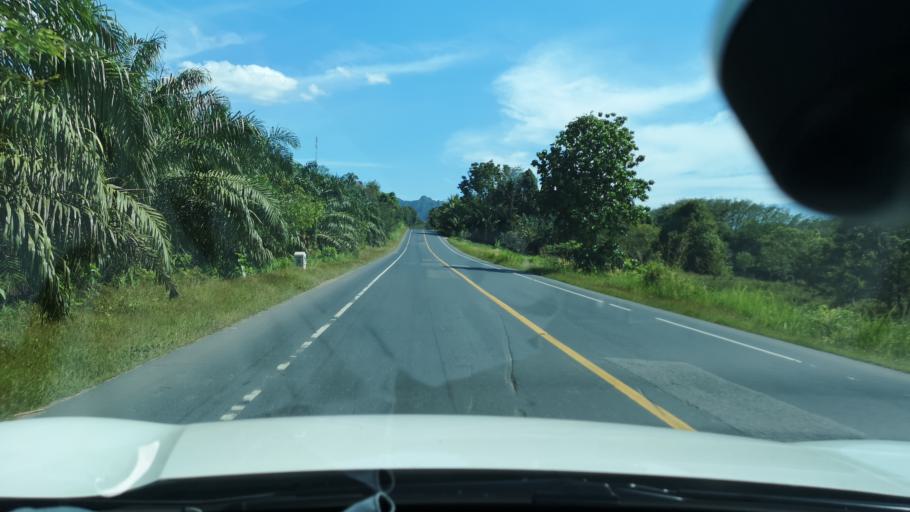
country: TH
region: Phangnga
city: Phang Nga
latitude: 8.5382
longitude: 98.4975
